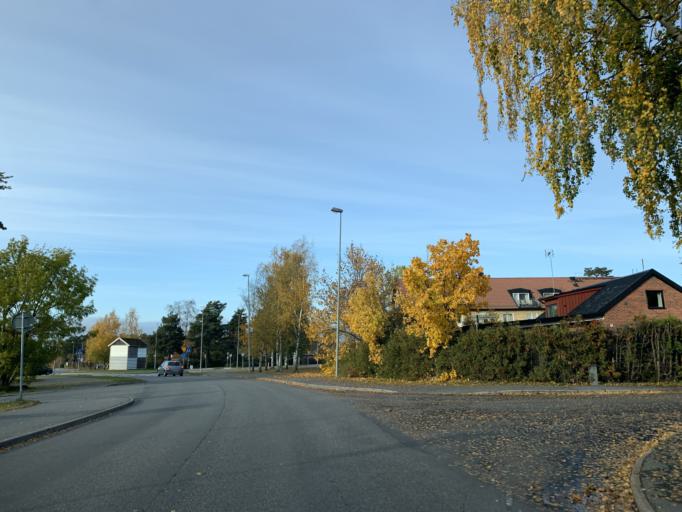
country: SE
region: Stockholm
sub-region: Haninge Kommun
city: Haninge
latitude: 59.1799
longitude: 18.1812
